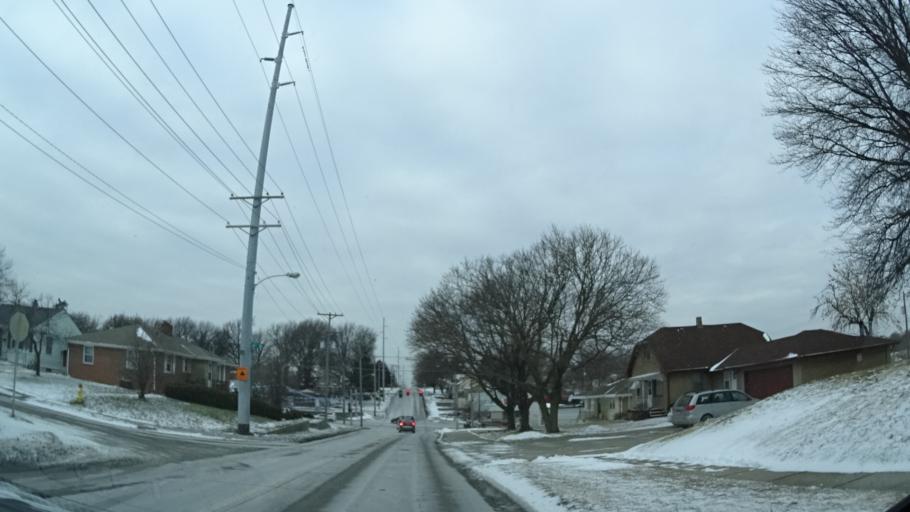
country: US
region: Nebraska
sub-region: Douglas County
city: Omaha
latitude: 41.2197
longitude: -95.9745
